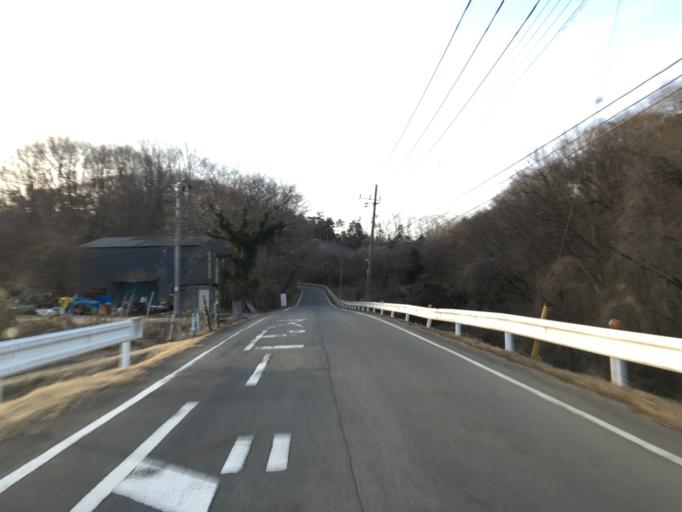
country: JP
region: Ibaraki
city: Daigo
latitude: 36.7971
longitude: 140.4041
